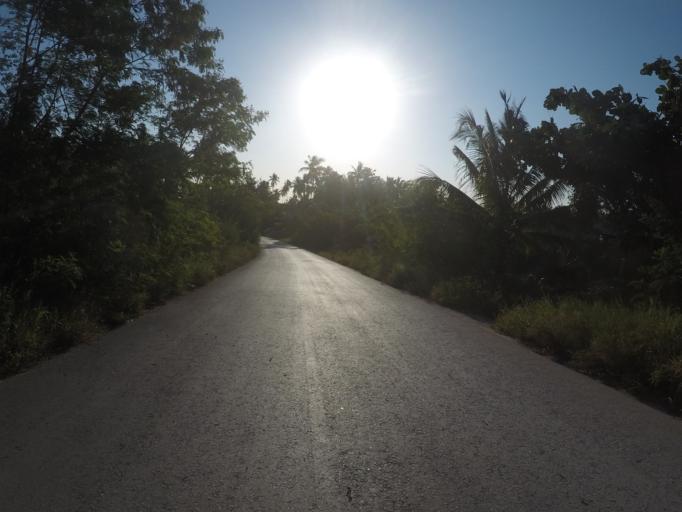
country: TZ
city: Kiwengwa
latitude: -6.1445
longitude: 39.4971
